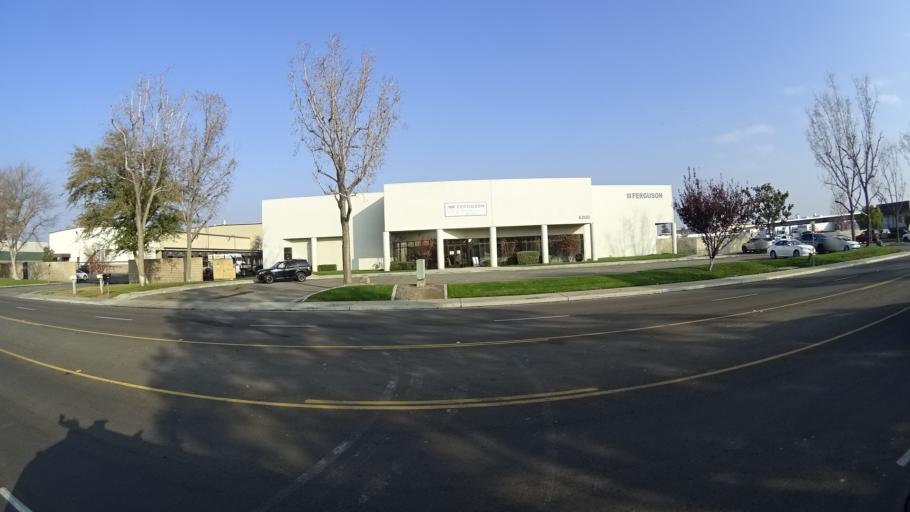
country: US
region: California
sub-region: Kern County
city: Greenacres
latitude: 35.3130
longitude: -119.0726
